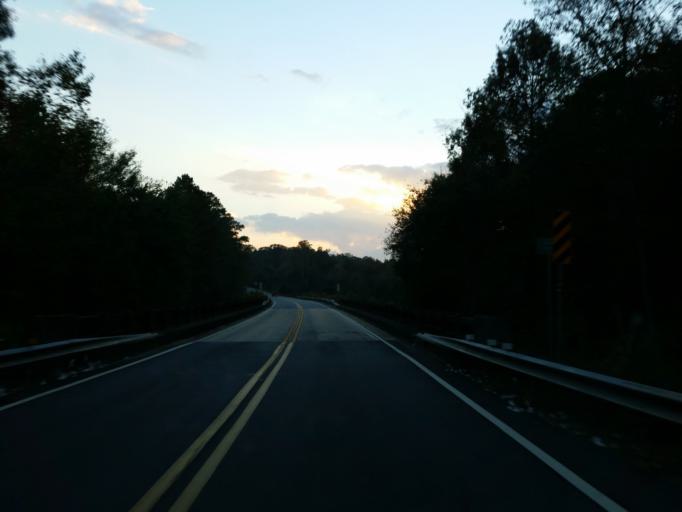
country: US
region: Georgia
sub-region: Pulaski County
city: Hawkinsville
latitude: 32.2196
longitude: -83.5259
